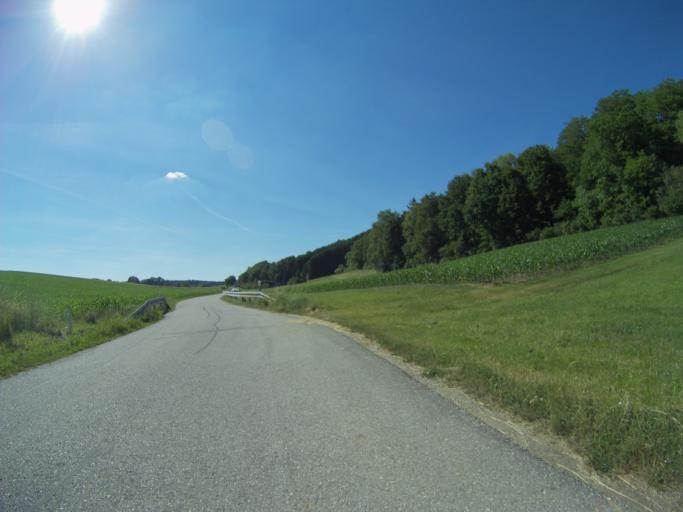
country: DE
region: Bavaria
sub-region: Upper Bavaria
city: Freising
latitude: 48.3958
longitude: 11.6890
